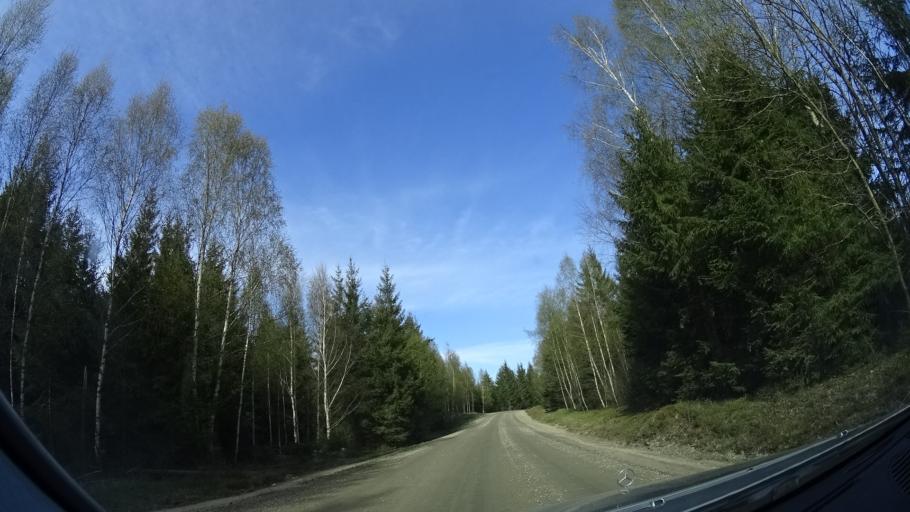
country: SE
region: Skane
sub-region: Hassleholms Kommun
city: Sosdala
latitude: 56.0870
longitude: 13.6793
